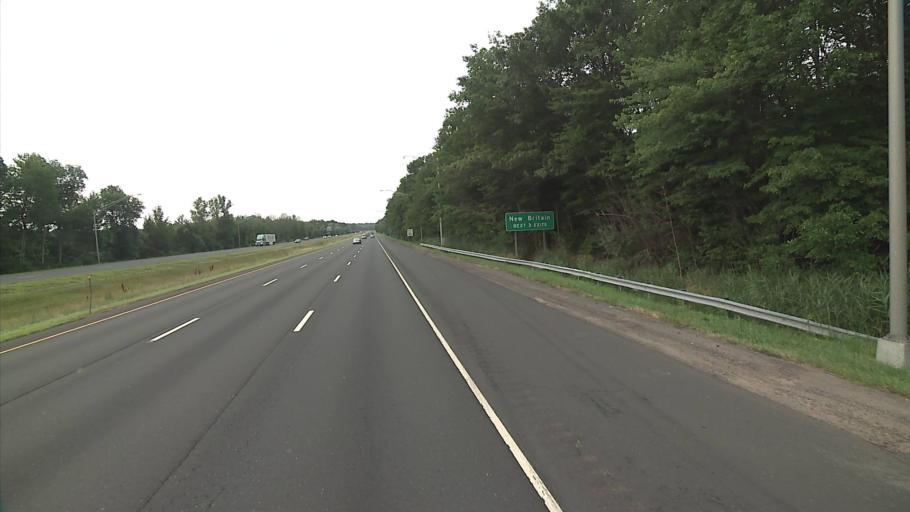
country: US
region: Connecticut
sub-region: Hartford County
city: Farmington
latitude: 41.7148
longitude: -72.7983
